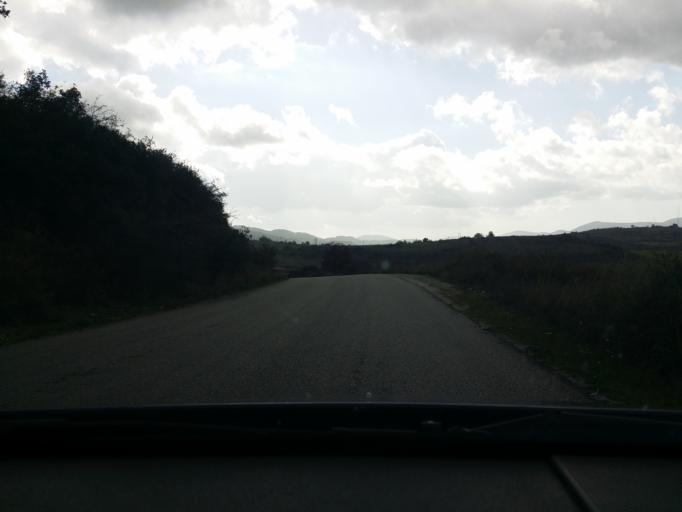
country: GR
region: West Greece
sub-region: Nomos Aitolias kai Akarnanias
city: Fitiai
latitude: 38.6907
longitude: 21.1786
